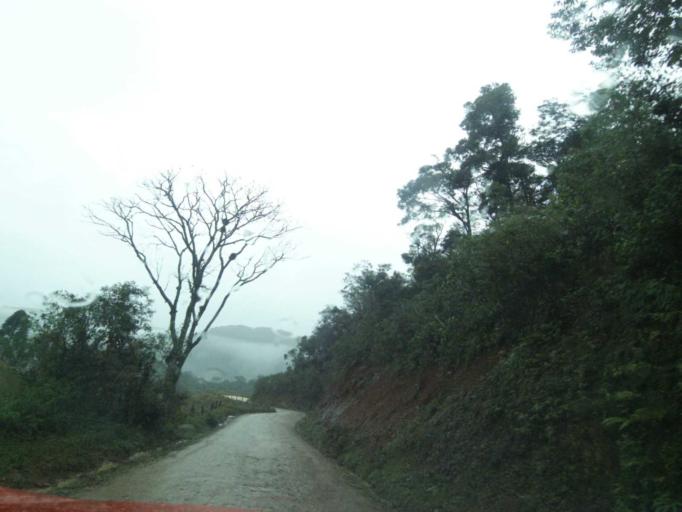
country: BR
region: Santa Catarina
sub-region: Anitapolis
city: Anitapolis
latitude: -27.9251
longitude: -49.1839
